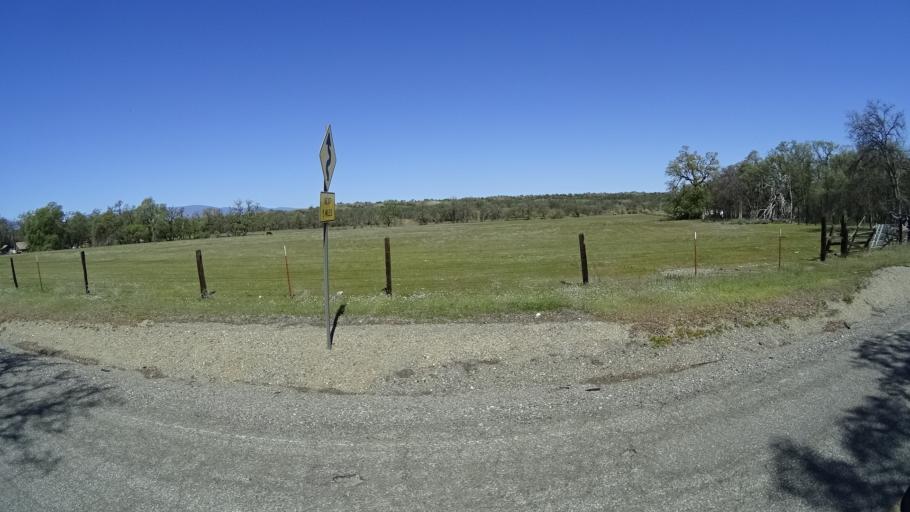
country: US
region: California
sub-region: Tehama County
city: Rancho Tehama Reserve
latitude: 39.7993
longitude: -122.4301
